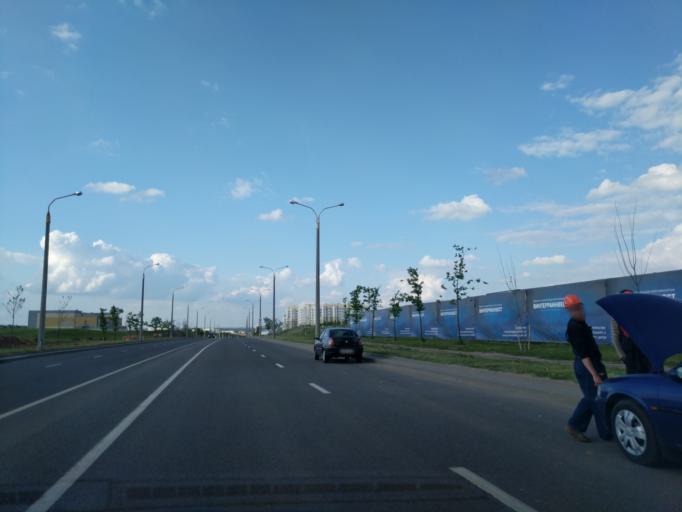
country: BY
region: Minsk
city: Zhdanovichy
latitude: 53.9194
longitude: 27.4176
